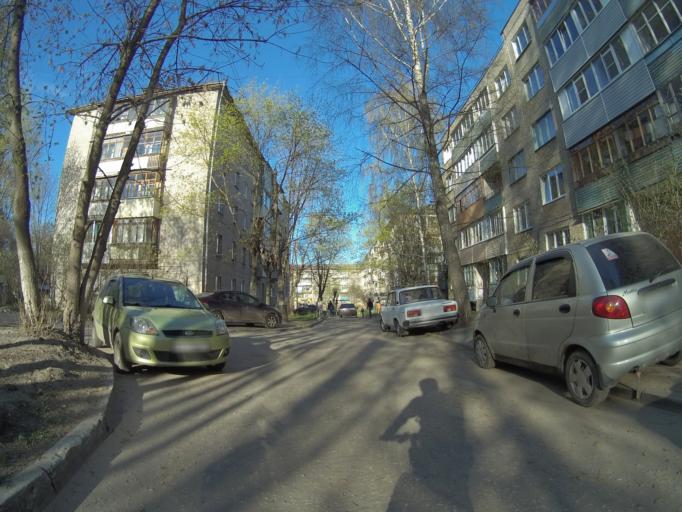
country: RU
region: Vladimir
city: Vladimir
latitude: 56.1479
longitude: 40.4129
